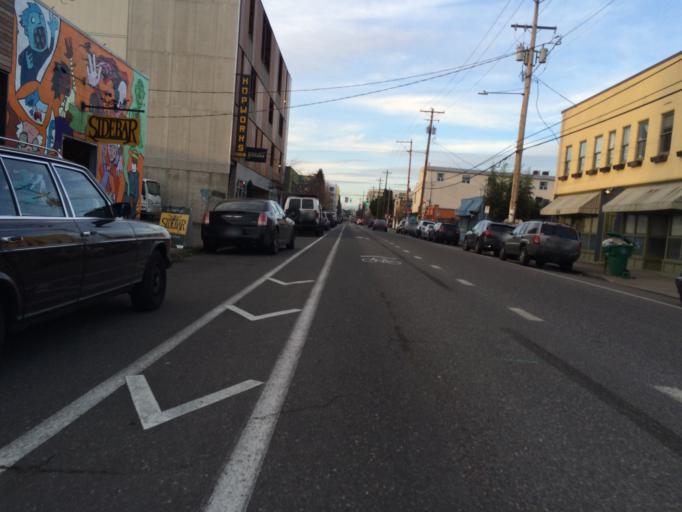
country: US
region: Oregon
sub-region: Multnomah County
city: Portland
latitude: 45.5510
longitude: -122.6667
